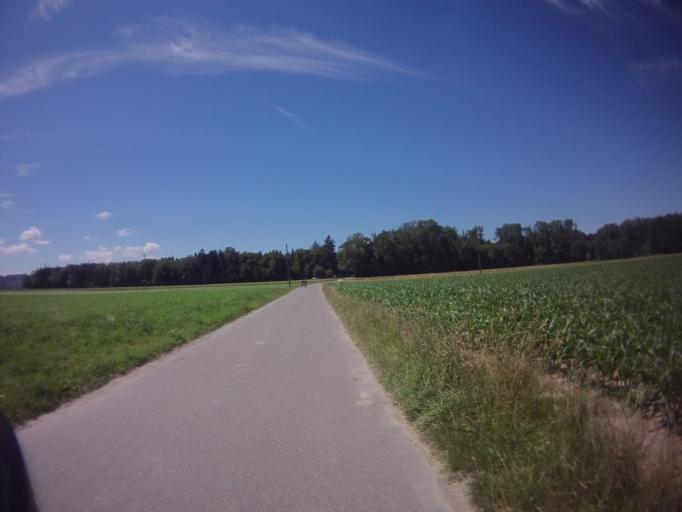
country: CH
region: Bern
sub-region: Emmental District
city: Kirchberg
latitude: 47.0800
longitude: 7.5667
